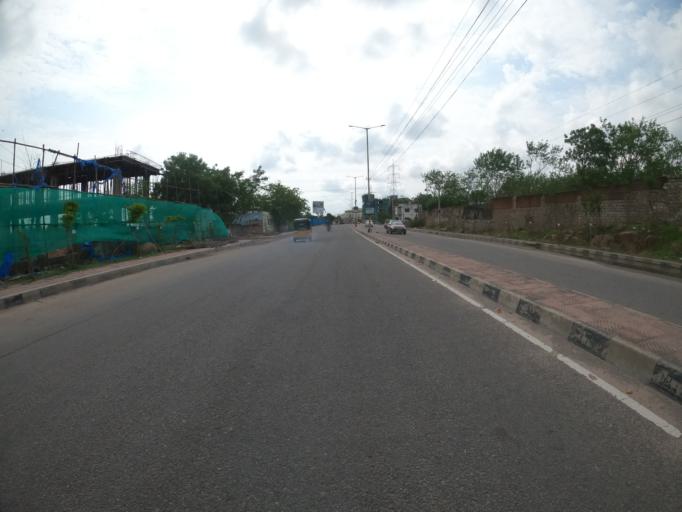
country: IN
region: Telangana
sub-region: Hyderabad
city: Hyderabad
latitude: 17.3817
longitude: 78.3660
